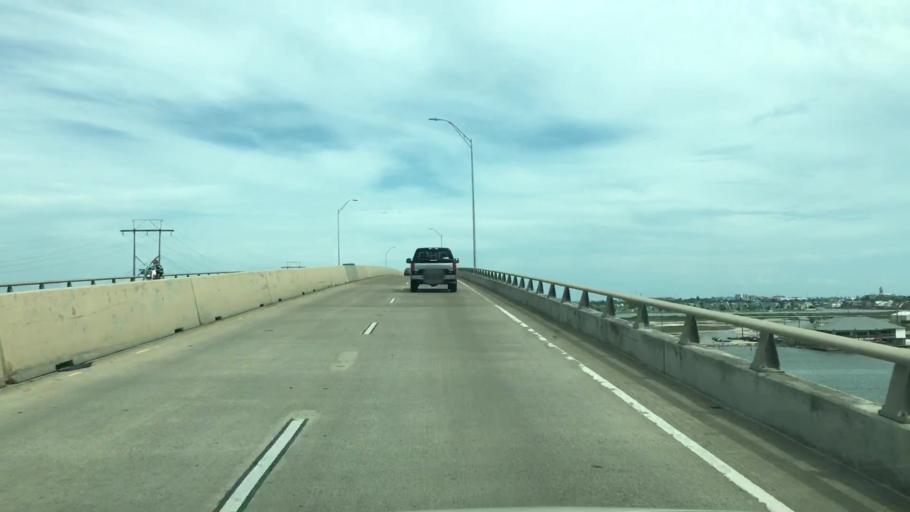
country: US
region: Texas
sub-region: Nueces County
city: Corpus Christi
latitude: 27.6358
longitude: -97.2422
